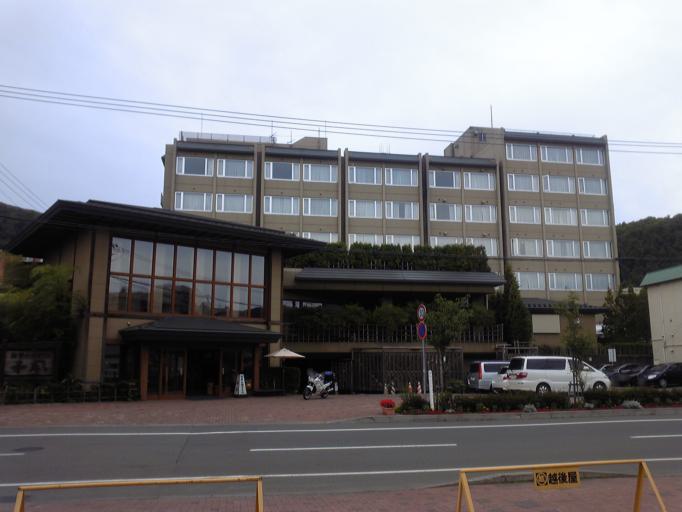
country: JP
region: Hokkaido
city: Date
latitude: 42.5641
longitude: 140.8247
